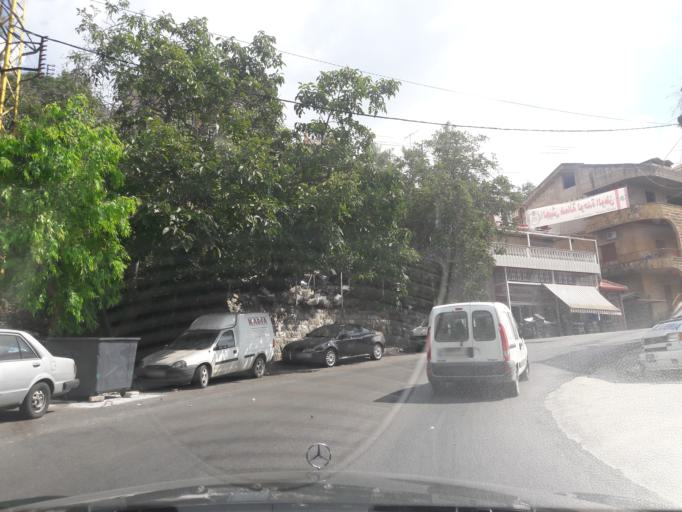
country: LB
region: Mont-Liban
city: Djounie
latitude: 33.9291
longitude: 35.6730
